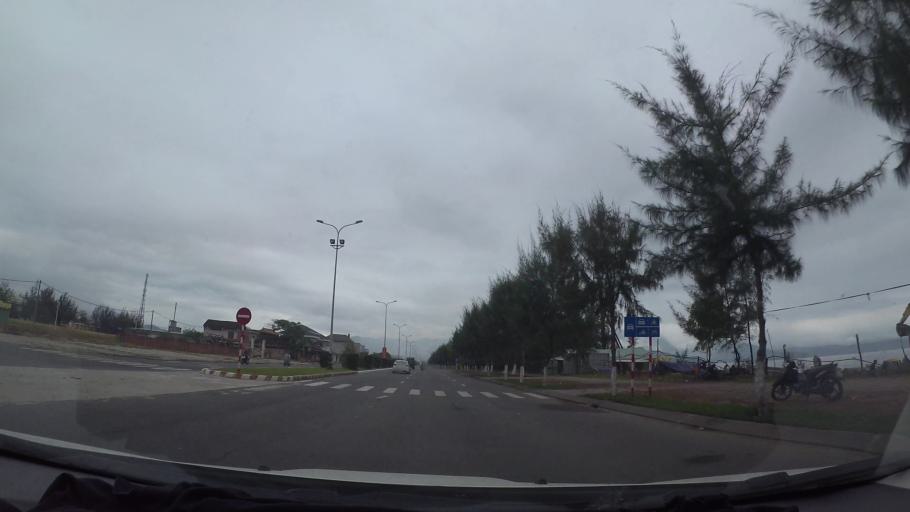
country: VN
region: Da Nang
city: Lien Chieu
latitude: 16.0991
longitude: 108.1419
